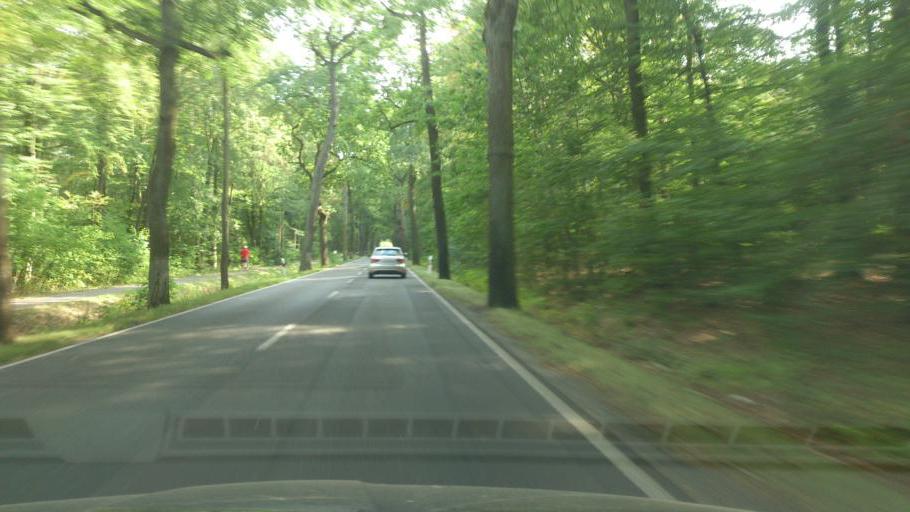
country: DE
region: Berlin
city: Wannsee
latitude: 52.3476
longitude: 13.1517
